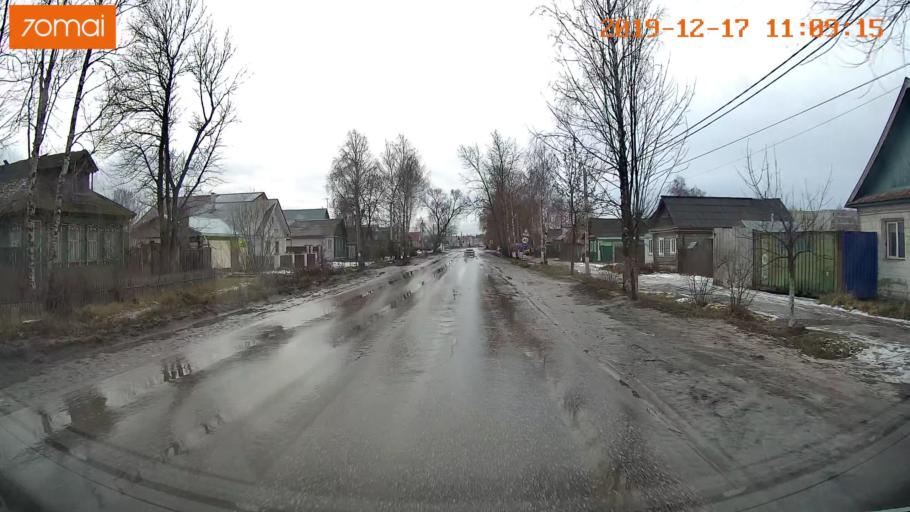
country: RU
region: Vladimir
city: Gus'-Khrustal'nyy
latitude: 55.6020
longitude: 40.6426
